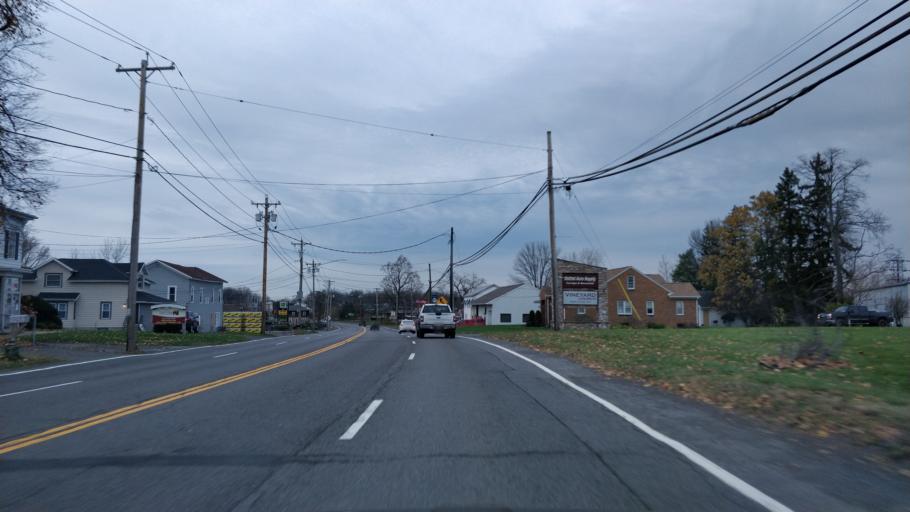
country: US
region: New York
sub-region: Onondaga County
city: North Syracuse
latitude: 43.1699
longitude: -76.1170
